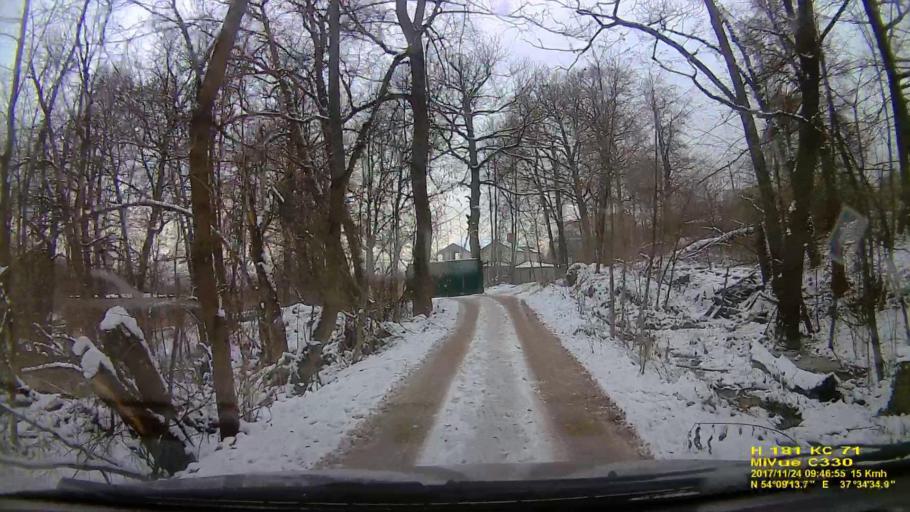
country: RU
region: Tula
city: Mendeleyevskiy
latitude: 54.1539
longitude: 37.5763
